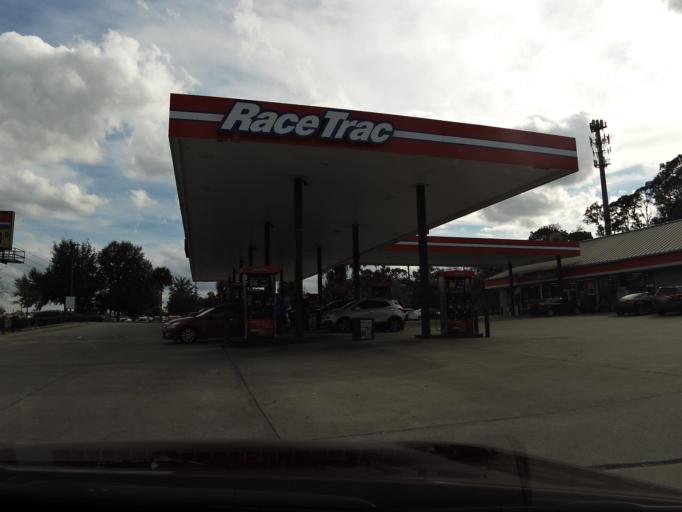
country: US
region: Florida
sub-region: Volusia County
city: De Land Southwest
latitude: 28.9915
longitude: -81.3026
